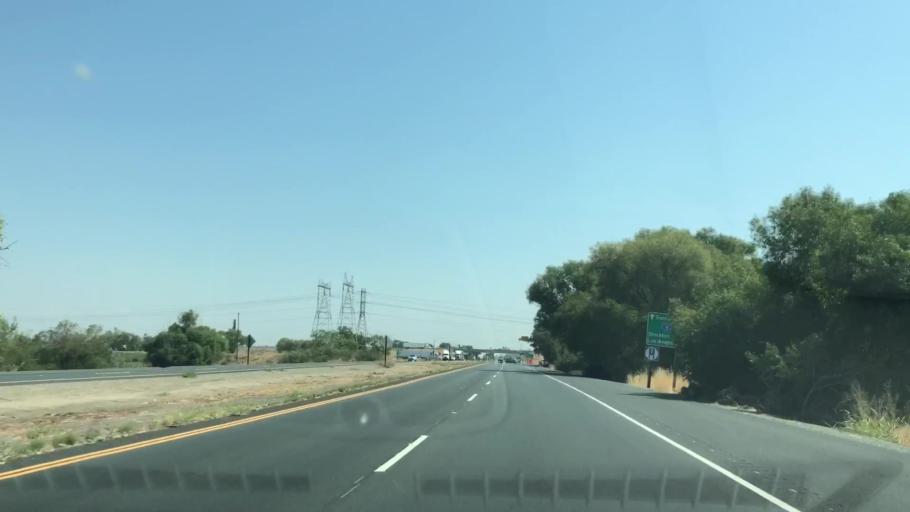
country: US
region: California
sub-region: San Joaquin County
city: Woodbridge
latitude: 38.1159
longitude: -121.4055
